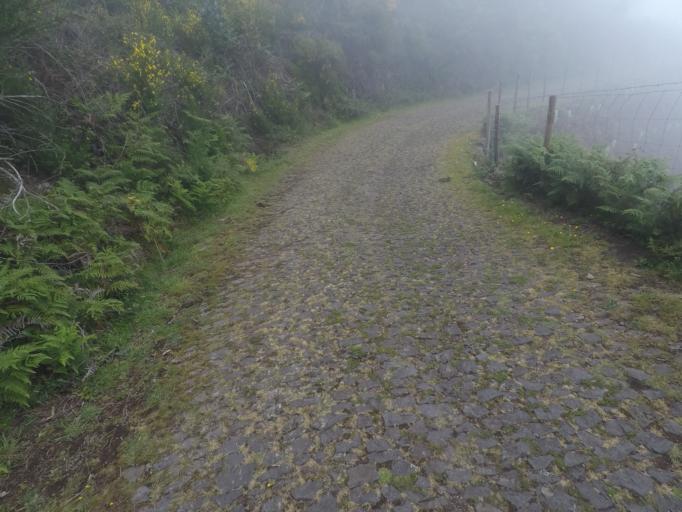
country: PT
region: Madeira
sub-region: Calheta
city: Arco da Calheta
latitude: 32.7309
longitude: -17.0971
